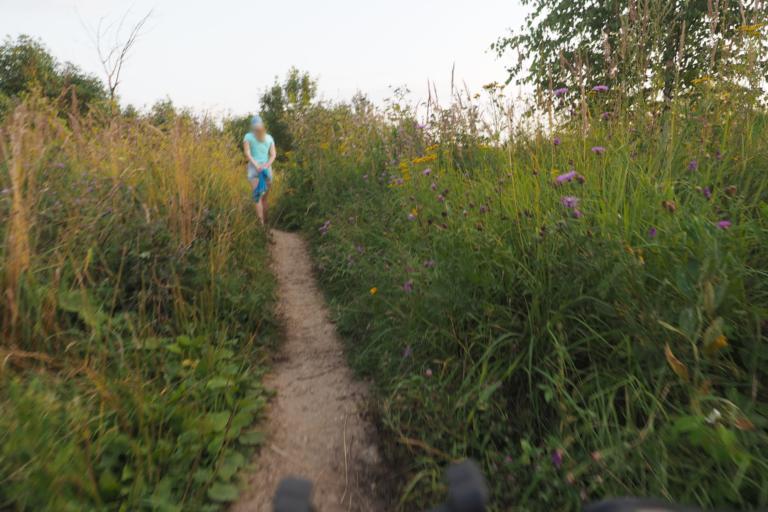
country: RU
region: Moscow
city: Orekhovo-Borisovo
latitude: 55.6019
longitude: 37.7054
